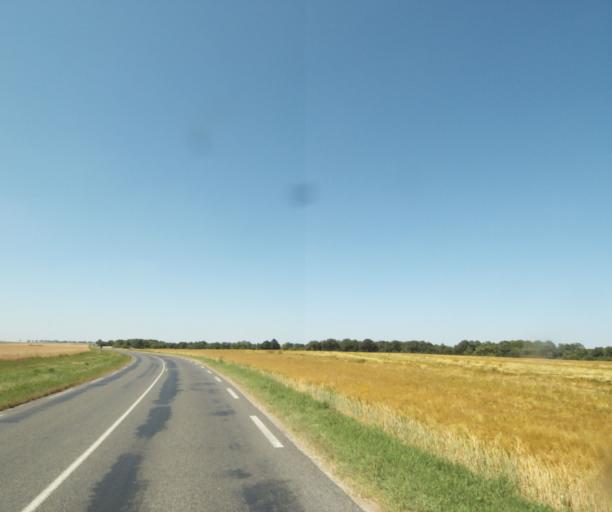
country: FR
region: Ile-de-France
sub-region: Departement de Seine-et-Marne
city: La Chapelle-la-Reine
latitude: 48.2867
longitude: 2.5798
